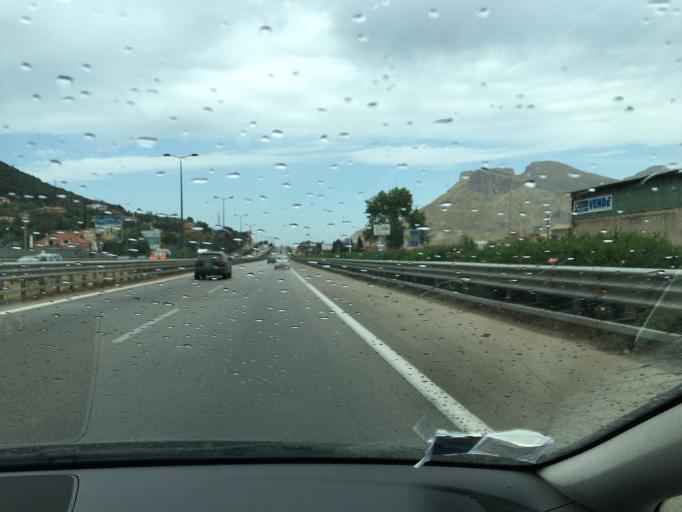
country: IT
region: Sicily
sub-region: Palermo
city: Isola delle Femmine
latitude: 38.1781
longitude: 13.2942
